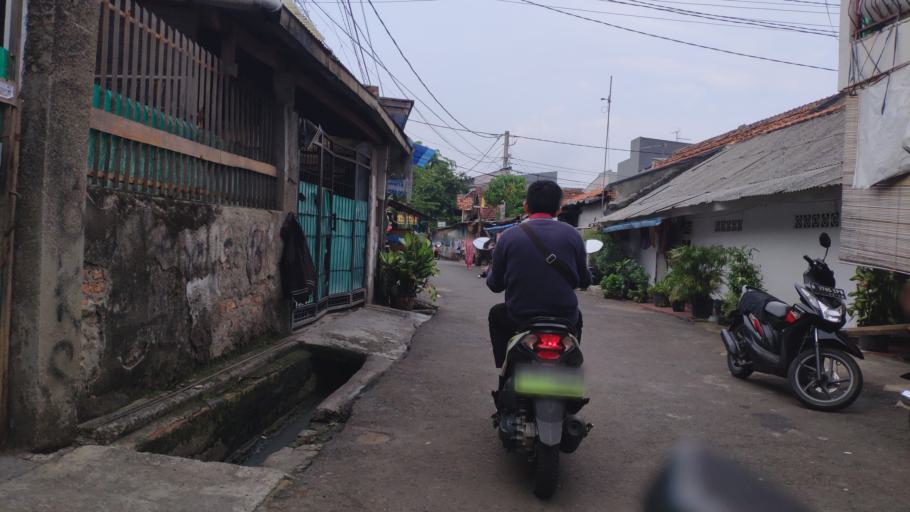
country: ID
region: Jakarta Raya
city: Jakarta
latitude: -6.2185
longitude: 106.8411
